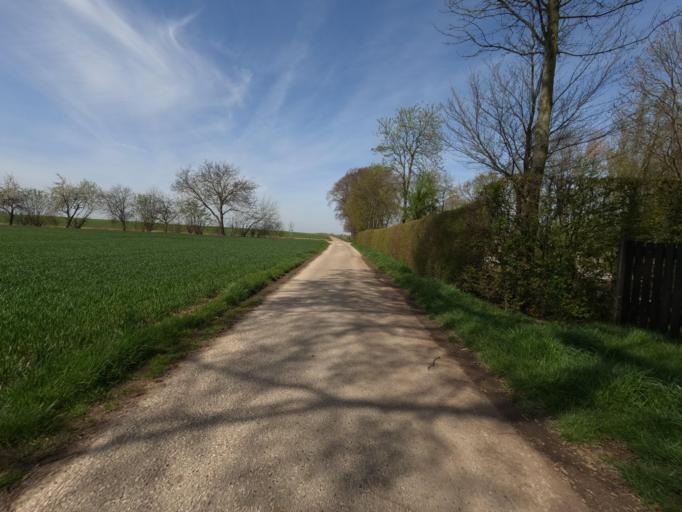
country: DE
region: North Rhine-Westphalia
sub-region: Regierungsbezirk Koln
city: Ubach-Palenberg
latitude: 50.9479
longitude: 6.1568
